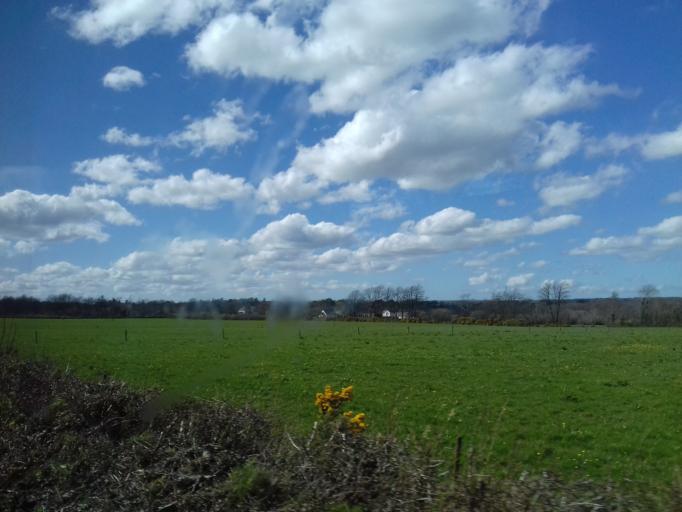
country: IE
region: Munster
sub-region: County Cork
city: Kanturk
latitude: 52.1292
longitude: -8.8402
